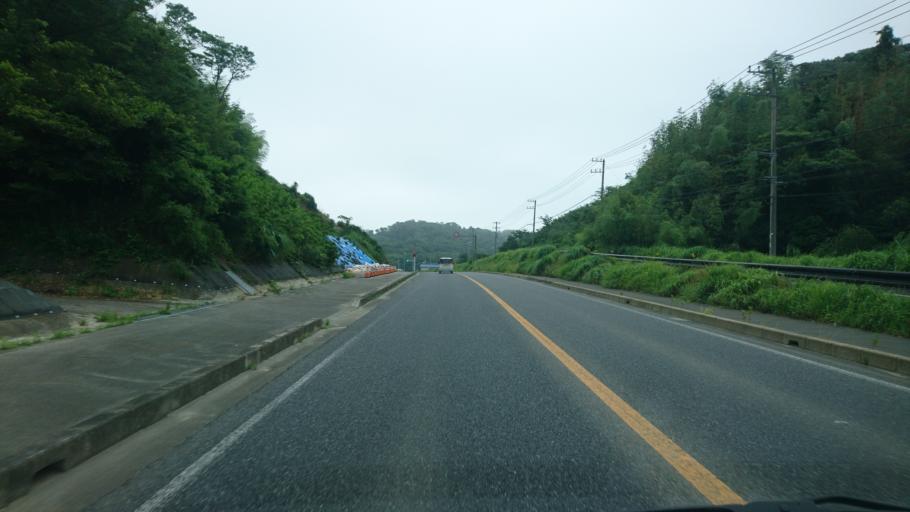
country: JP
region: Chiba
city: Kimitsu
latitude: 35.2550
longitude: 139.8841
